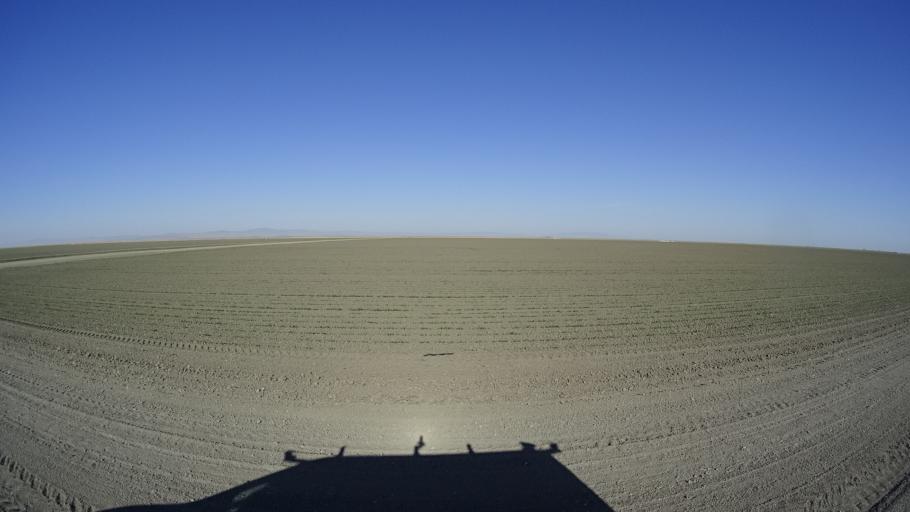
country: US
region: California
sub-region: Kings County
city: Stratford
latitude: 36.1022
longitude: -119.7979
